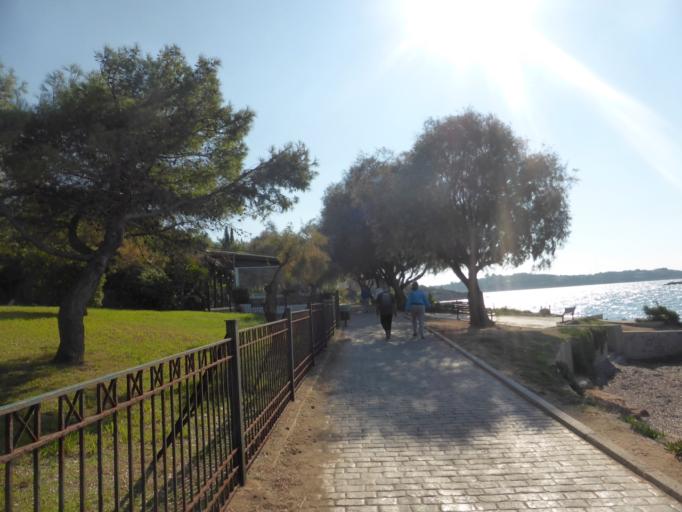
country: GR
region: Attica
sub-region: Nomarchia Anatolikis Attikis
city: Vouliagmeni
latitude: 37.8271
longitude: 23.7700
